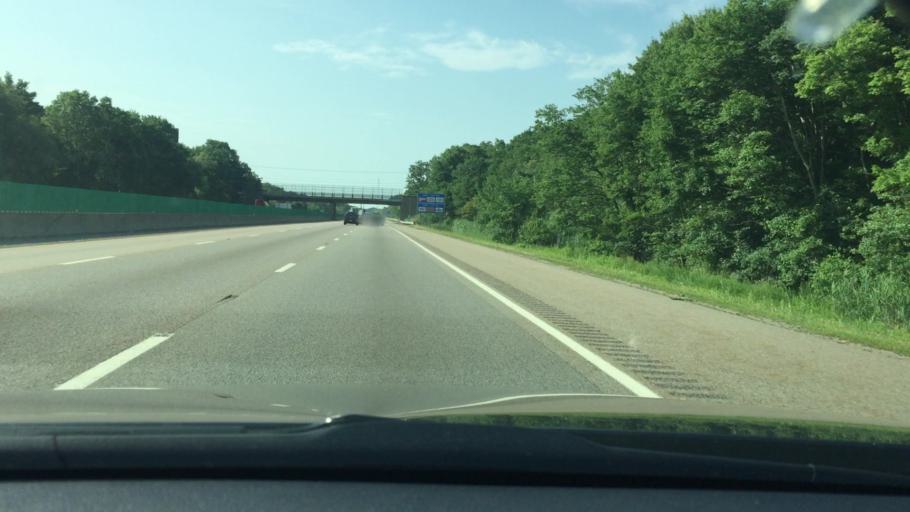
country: US
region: Massachusetts
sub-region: Plymouth County
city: West Bridgewater
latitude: 42.0435
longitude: -71.0556
